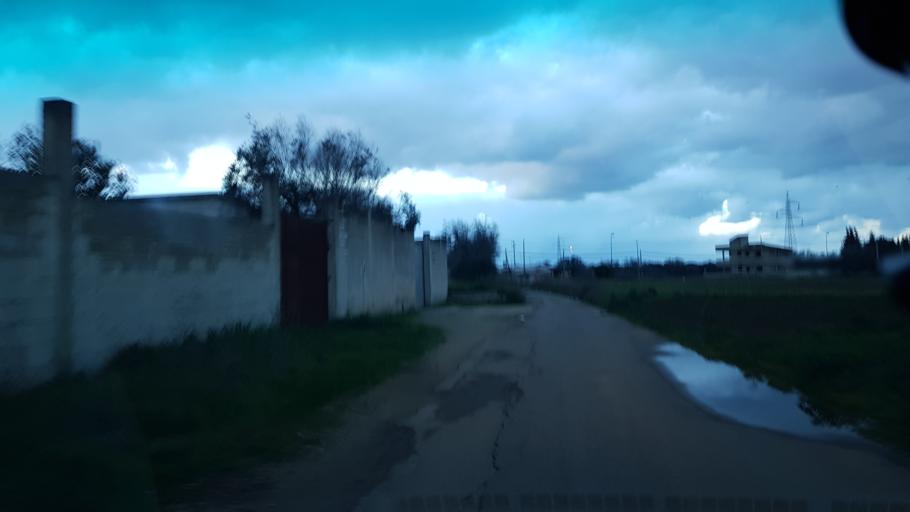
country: IT
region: Apulia
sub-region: Provincia di Brindisi
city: Torchiarolo
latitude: 40.4897
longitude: 18.0543
